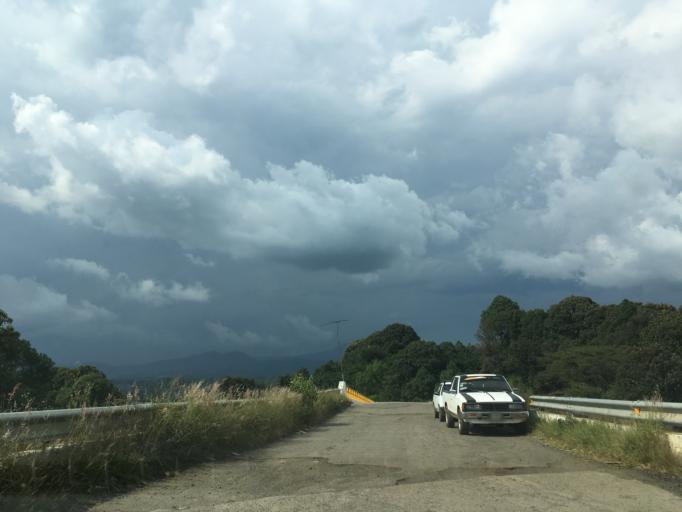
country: MX
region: Michoacan
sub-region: Ziracuaretiro
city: Patuan
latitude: 19.4408
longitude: -101.8813
